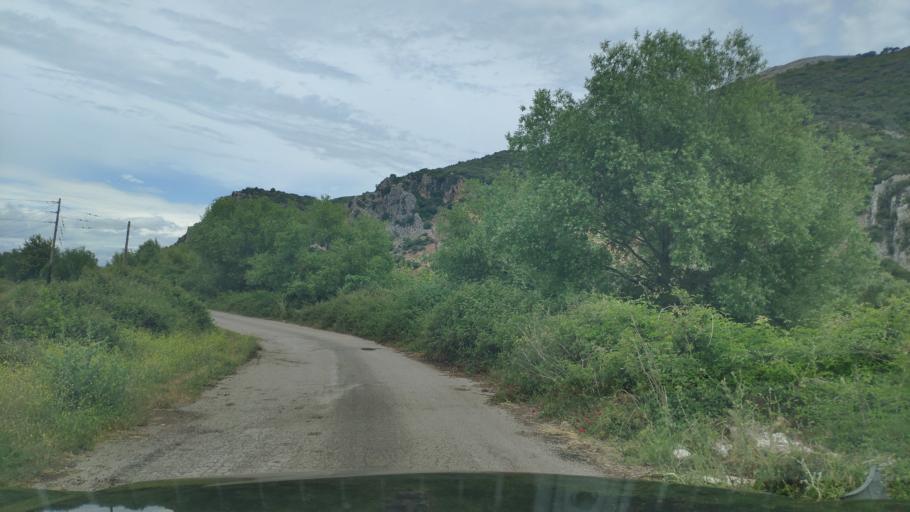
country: GR
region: West Greece
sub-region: Nomos Aitolias kai Akarnanias
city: Vonitsa
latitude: 38.9127
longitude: 20.9082
